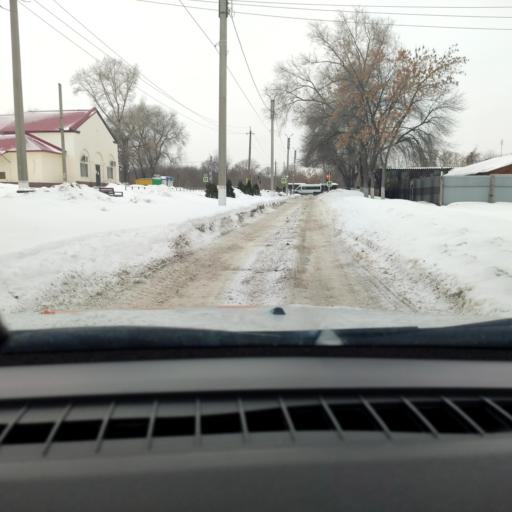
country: RU
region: Samara
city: Novokuybyshevsk
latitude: 53.1148
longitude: 49.9342
